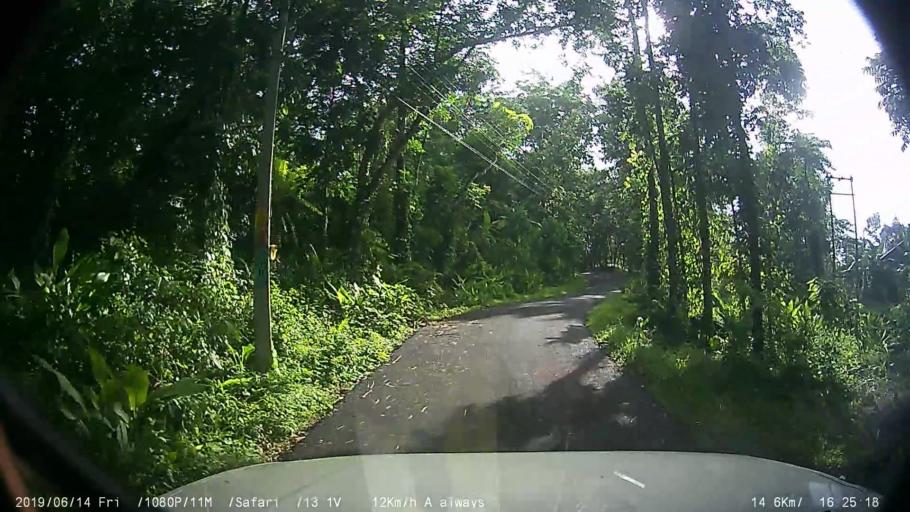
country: IN
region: Kerala
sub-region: Kottayam
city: Palackattumala
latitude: 9.7753
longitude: 76.5957
